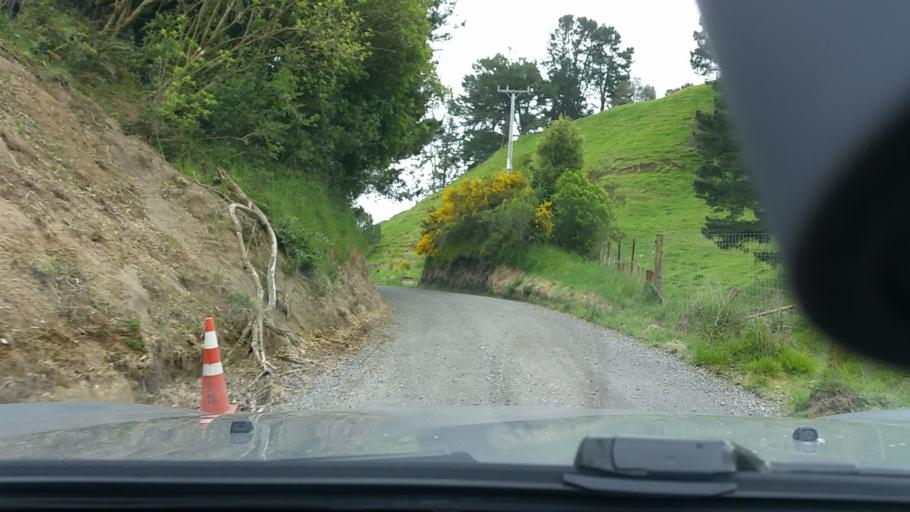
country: NZ
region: Bay of Plenty
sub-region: Rotorua District
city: Rotorua
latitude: -38.4021
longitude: 176.1820
